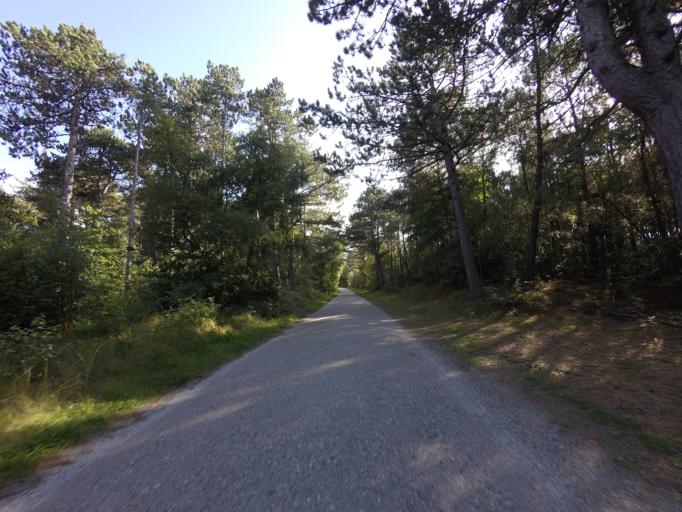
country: NL
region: Friesland
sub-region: Gemeente Terschelling
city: West-Terschelling
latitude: 53.3786
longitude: 5.2194
